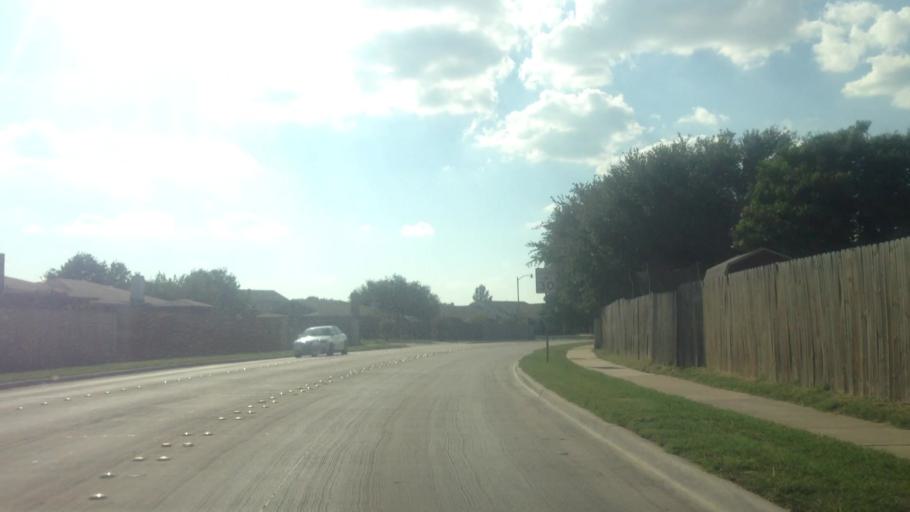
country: US
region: Texas
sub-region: Tarrant County
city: Watauga
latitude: 32.8851
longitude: -97.2552
